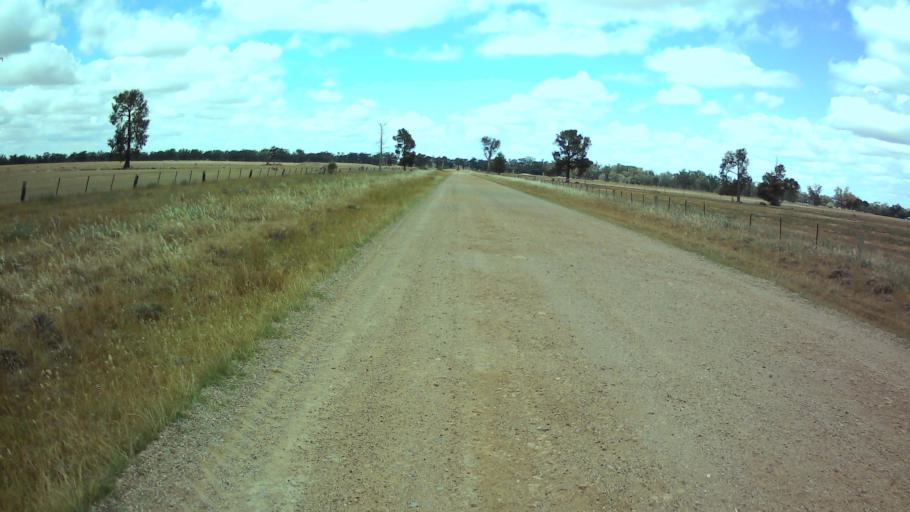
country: AU
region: New South Wales
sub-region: Weddin
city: Grenfell
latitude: -34.0229
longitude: 147.9141
